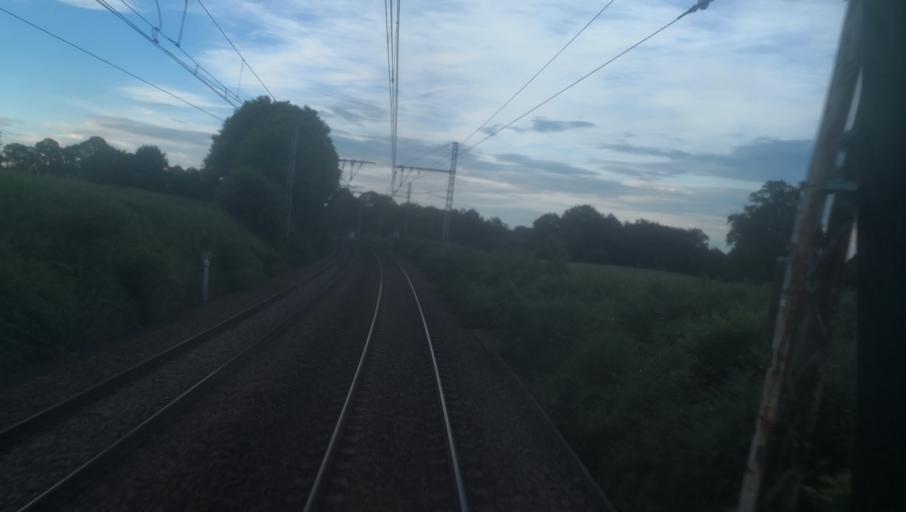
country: FR
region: Limousin
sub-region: Departement de la Creuse
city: Saint-Agnant-de-Versillat
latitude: 46.2997
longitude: 1.5021
